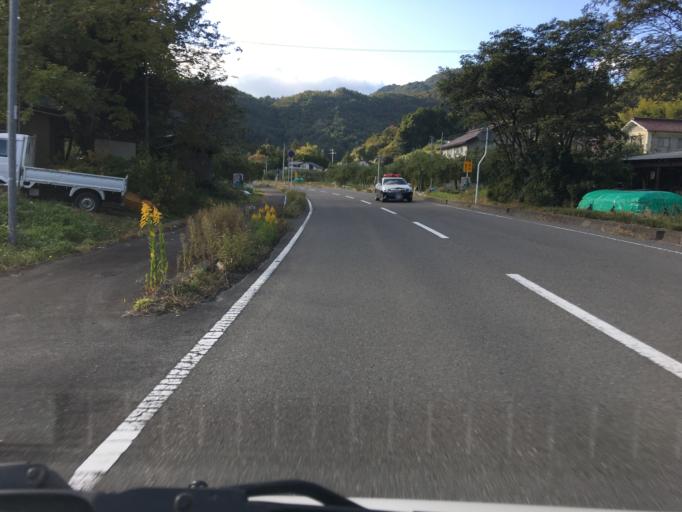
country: JP
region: Fukushima
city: Fukushima-shi
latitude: 37.8437
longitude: 140.4419
